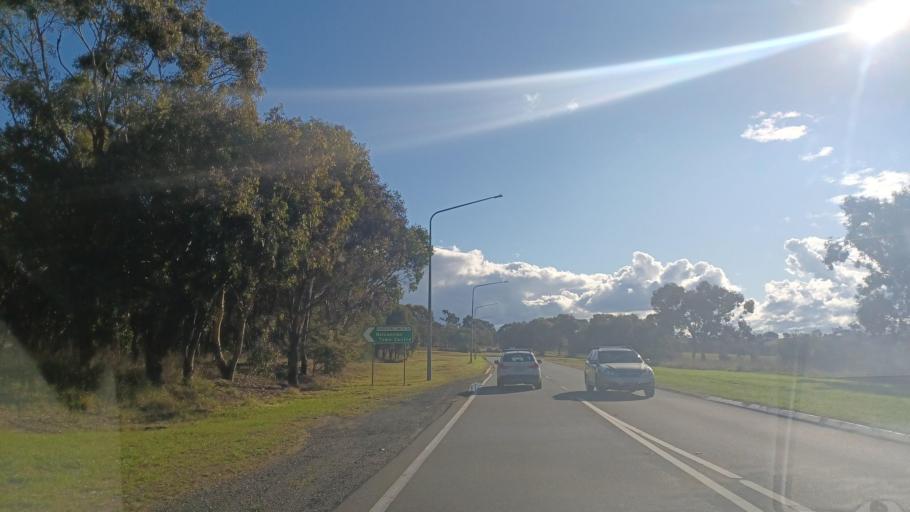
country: AU
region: Australian Capital Territory
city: Belconnen
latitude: -35.1924
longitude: 149.0651
